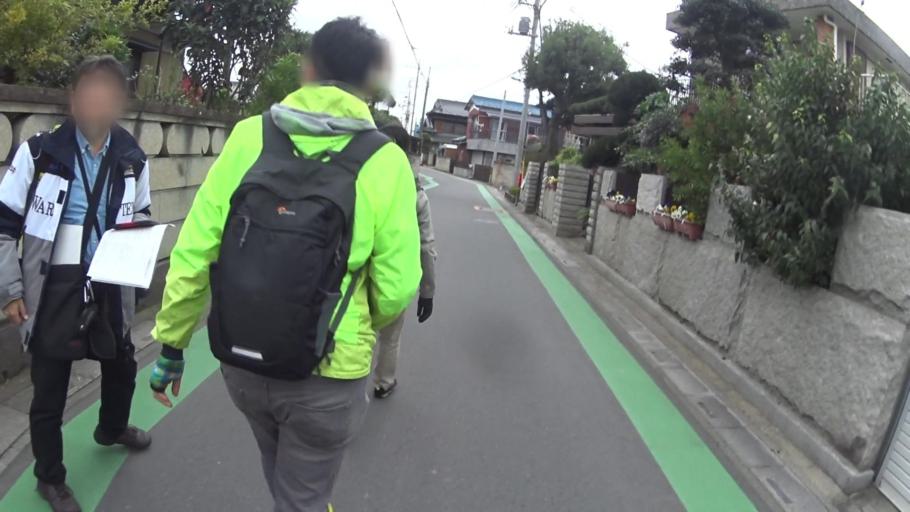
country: JP
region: Saitama
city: Yashio-shi
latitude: 35.8293
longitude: 139.8486
